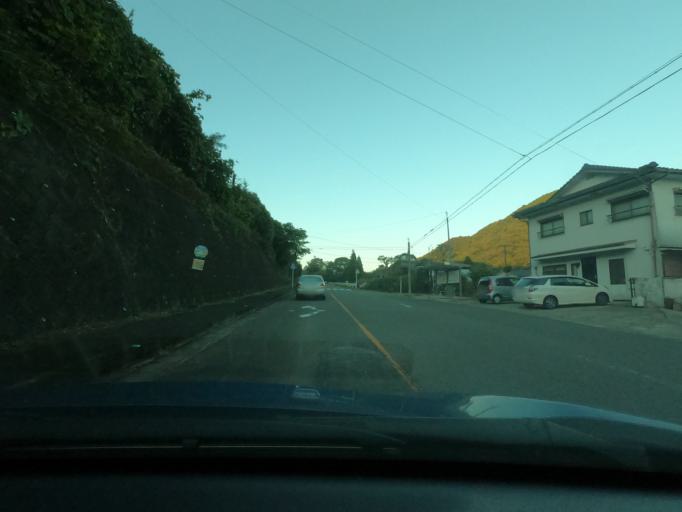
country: JP
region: Kagoshima
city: Satsumasendai
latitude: 31.8010
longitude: 130.4799
